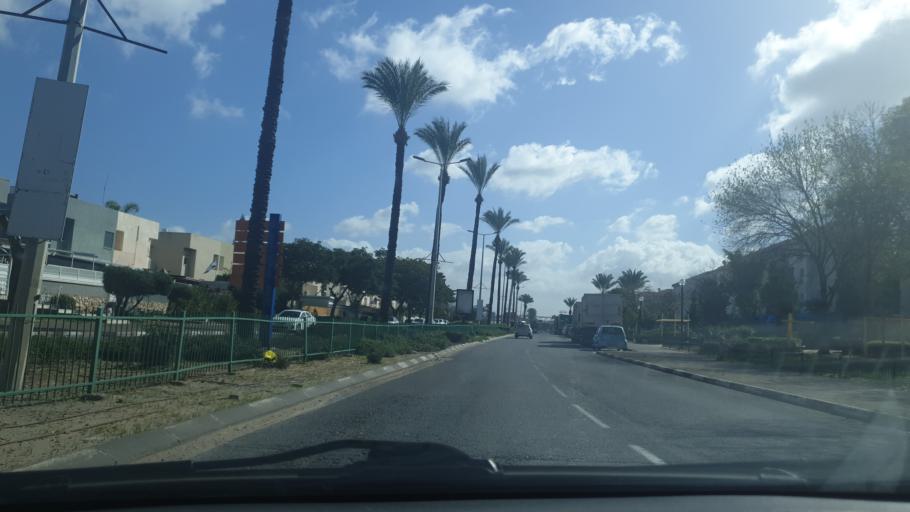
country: IL
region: Haifa
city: Qesarya
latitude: 32.5026
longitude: 34.9215
